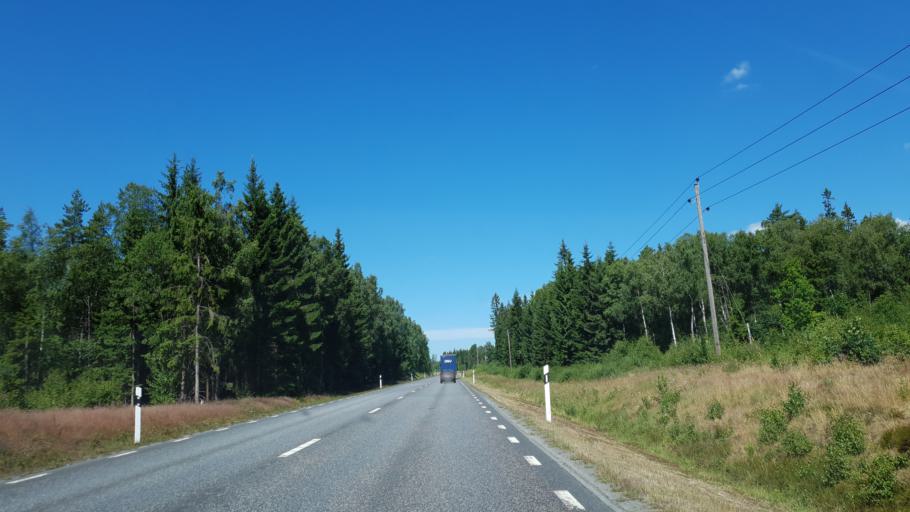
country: SE
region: Joenkoeping
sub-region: Varnamo Kommun
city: Rydaholm
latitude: 57.0378
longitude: 14.2431
